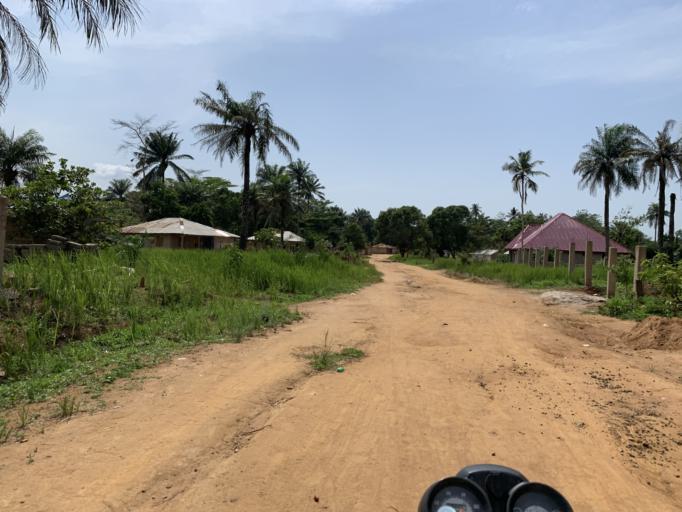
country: SL
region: Western Area
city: Waterloo
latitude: 8.3612
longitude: -13.0457
